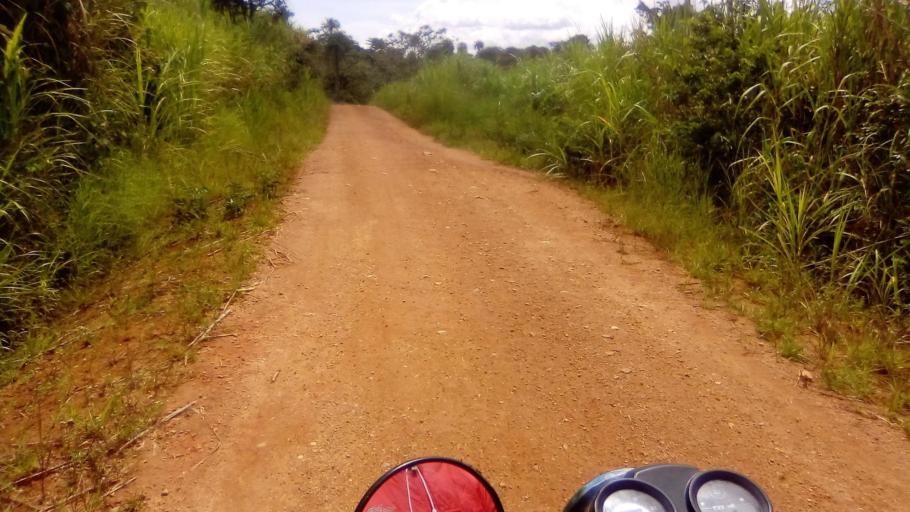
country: SL
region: Eastern Province
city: Simbakoro
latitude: 8.5429
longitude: -10.9368
